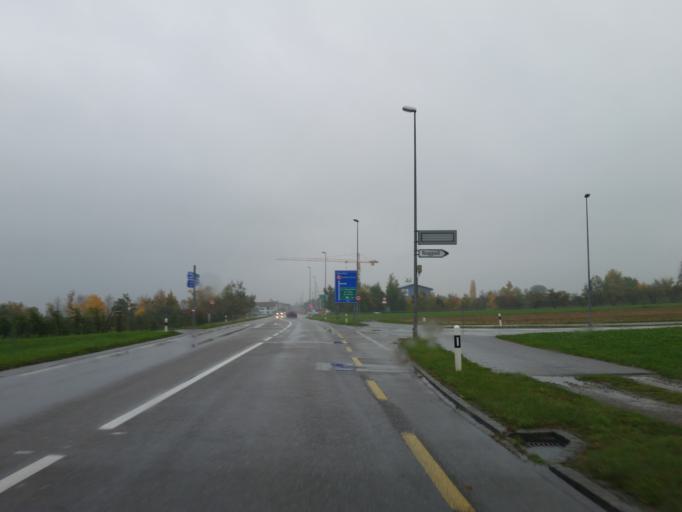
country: CH
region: Thurgau
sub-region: Arbon District
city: Roggwil
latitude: 47.5238
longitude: 9.3952
